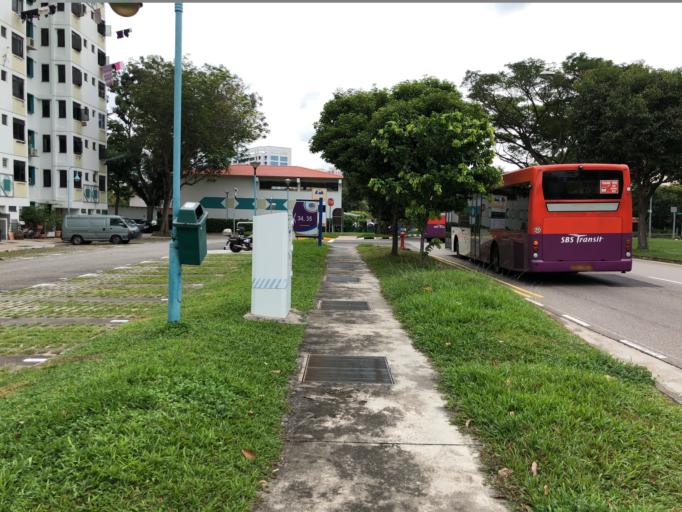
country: SG
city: Singapore
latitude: 1.3271
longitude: 103.8581
